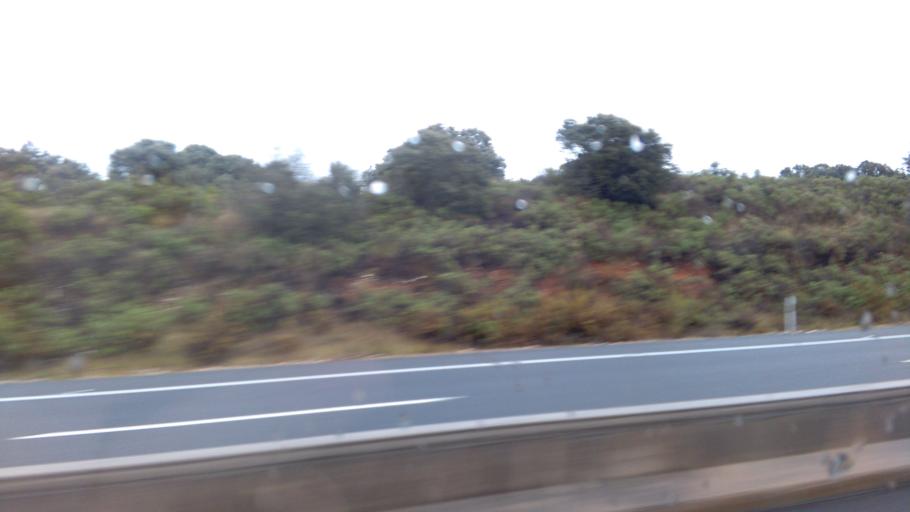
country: ES
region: Extremadura
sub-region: Provincia de Caceres
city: Casas de Miravete
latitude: 39.7697
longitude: -5.7372
